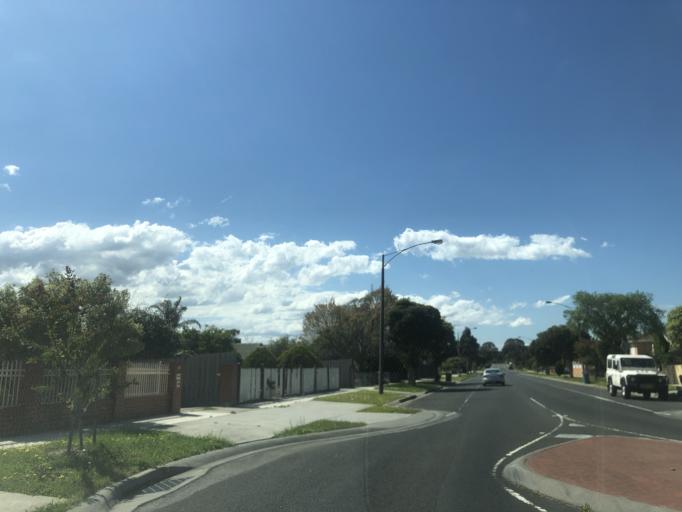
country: AU
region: Victoria
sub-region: Casey
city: Endeavour Hills
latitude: -37.9859
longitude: 145.2655
